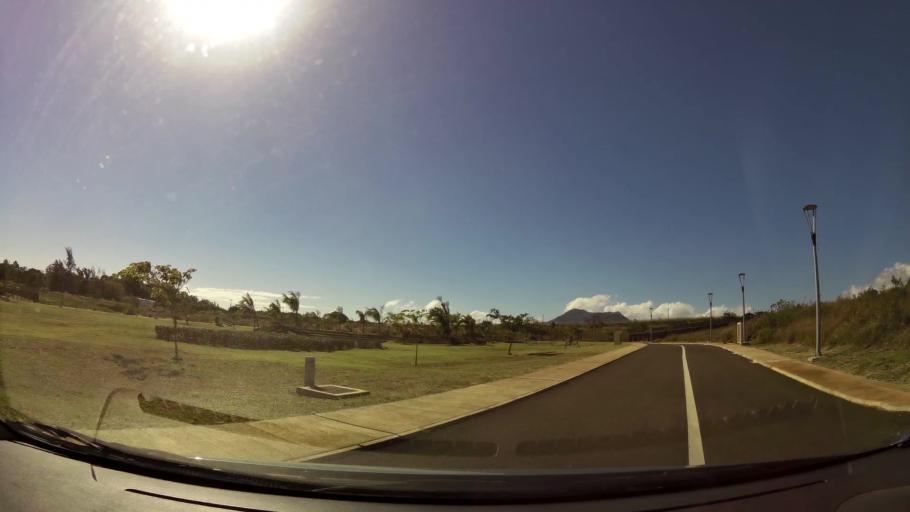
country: MU
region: Black River
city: Flic en Flac
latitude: -20.2696
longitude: 57.3850
